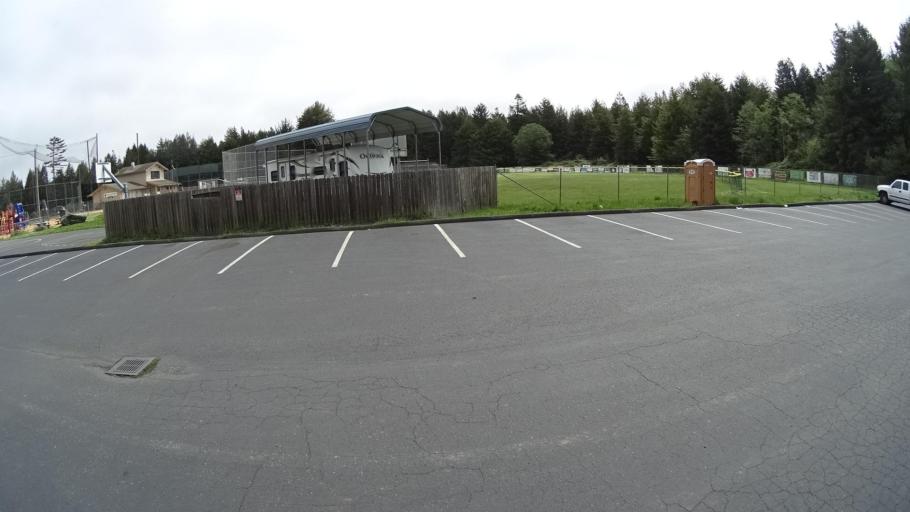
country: US
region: California
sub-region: Humboldt County
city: Cutten
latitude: 40.7691
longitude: -124.1391
